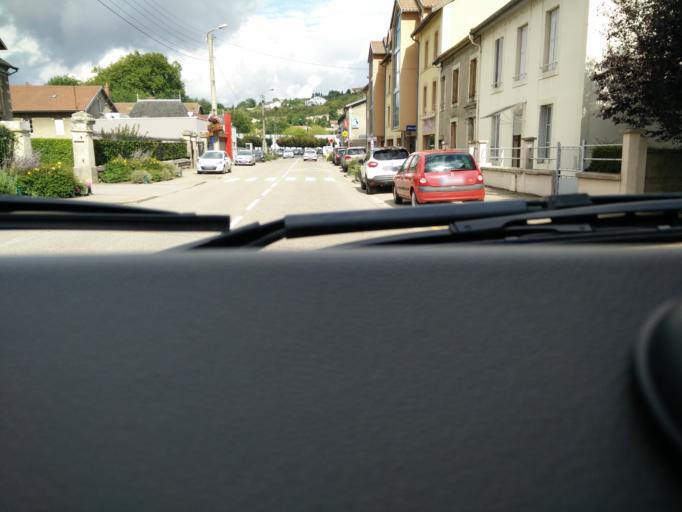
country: FR
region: Lorraine
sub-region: Departement de la Meuse
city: Verdun
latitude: 49.1739
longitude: 5.3815
